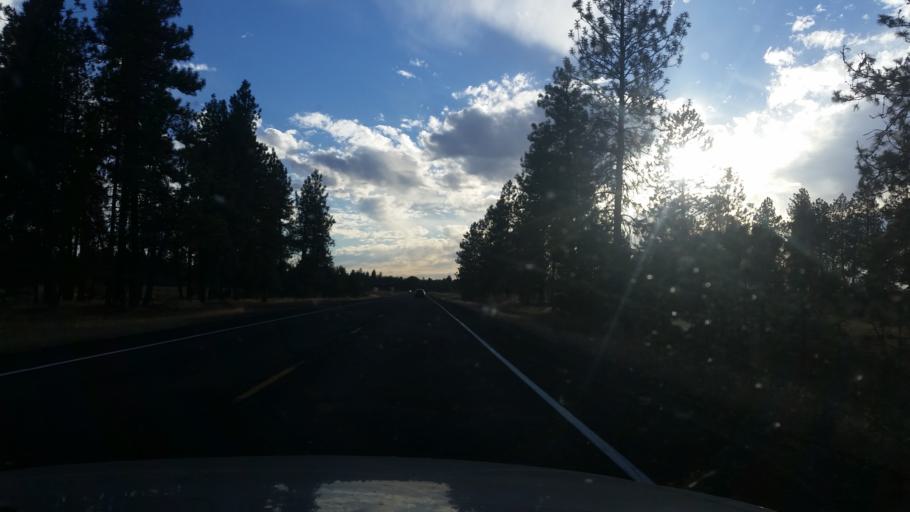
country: US
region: Washington
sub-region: Spokane County
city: Medical Lake
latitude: 47.4423
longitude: -117.7541
